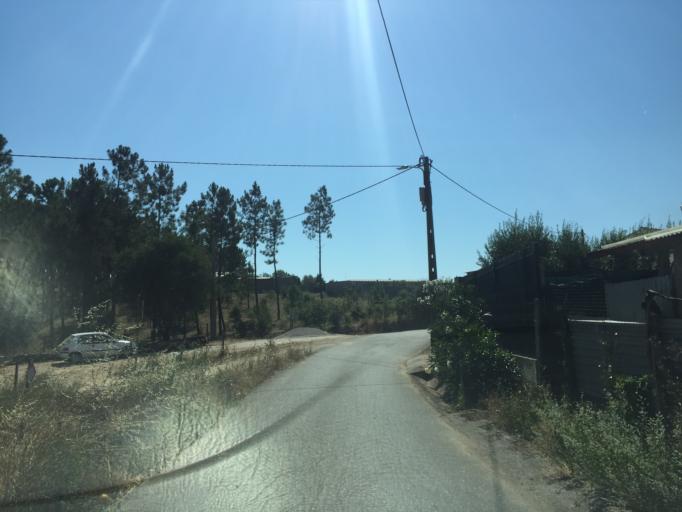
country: PT
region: Santarem
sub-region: Constancia
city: Constancia
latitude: 39.5372
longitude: -8.3161
